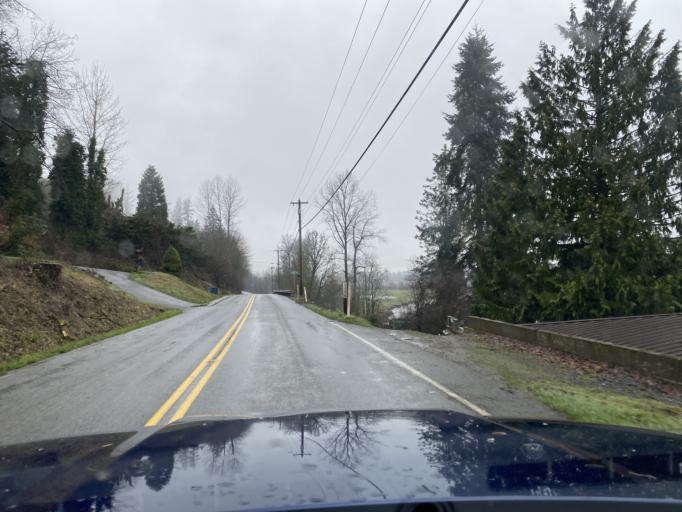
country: US
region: Washington
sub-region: King County
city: Duvall
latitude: 47.7943
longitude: -122.0005
